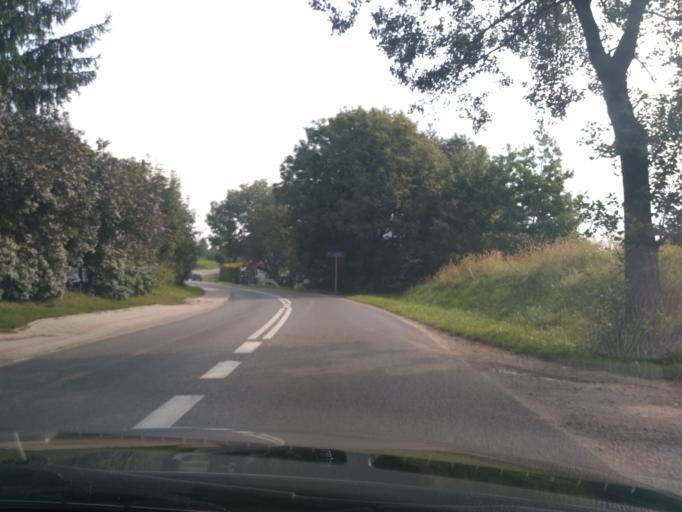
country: PL
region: Subcarpathian Voivodeship
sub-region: Powiat rzeszowski
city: Boguchwala
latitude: 50.0030
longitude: 21.9385
